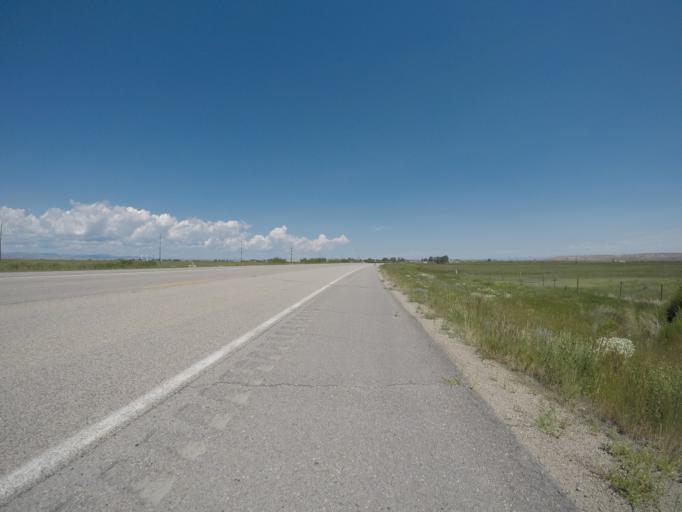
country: US
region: Wyoming
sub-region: Sublette County
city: Marbleton
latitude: 42.5278
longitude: -110.1097
